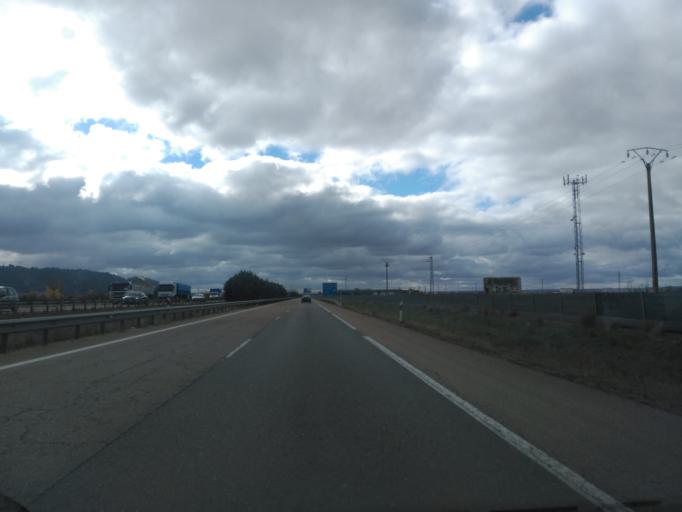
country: ES
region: Castille and Leon
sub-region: Provincia de Valladolid
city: Cabezon
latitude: 41.7653
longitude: -4.6273
